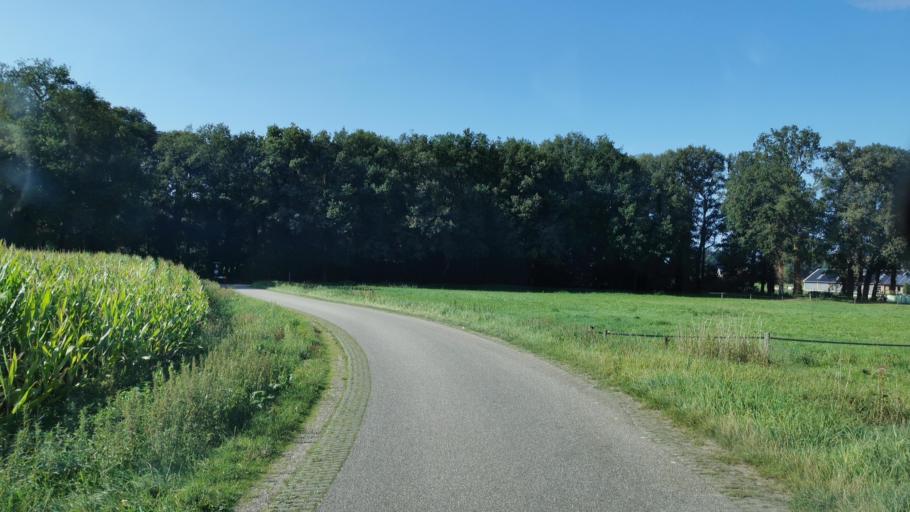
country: DE
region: Lower Saxony
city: Lage
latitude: 52.4027
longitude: 6.9471
